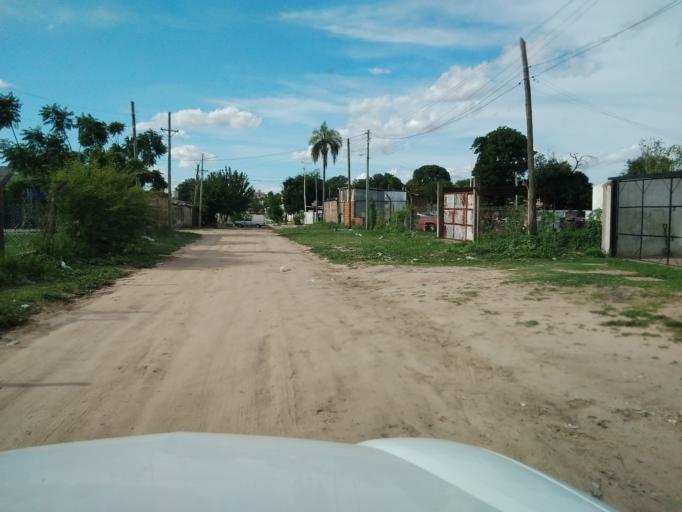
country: AR
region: Corrientes
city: Corrientes
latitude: -27.4830
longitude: -58.8508
